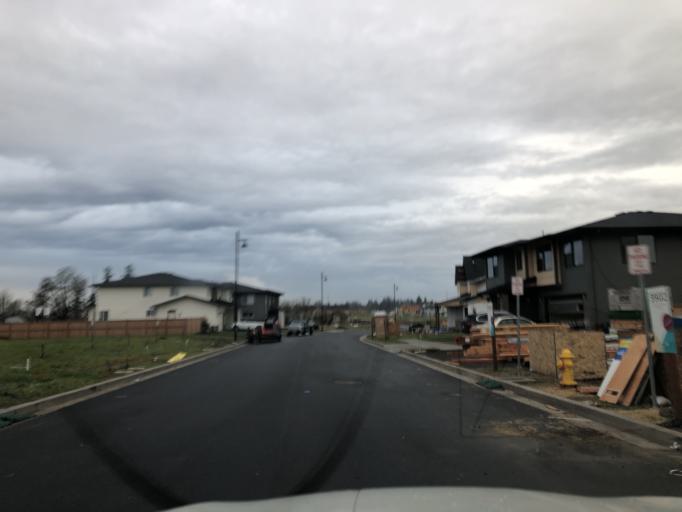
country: US
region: Oregon
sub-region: Washington County
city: Aloha
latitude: 45.4917
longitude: -122.9115
